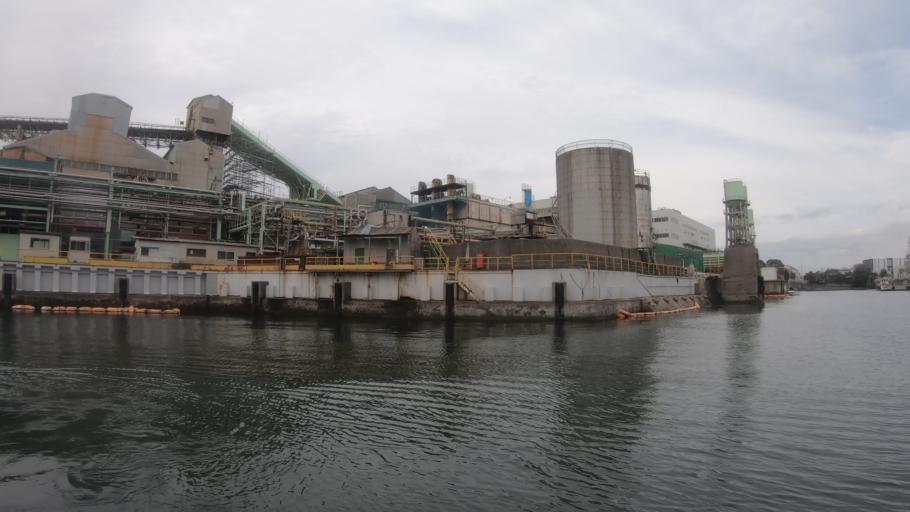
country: JP
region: Kanagawa
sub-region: Kawasaki-shi
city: Kawasaki
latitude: 35.4921
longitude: 139.6884
